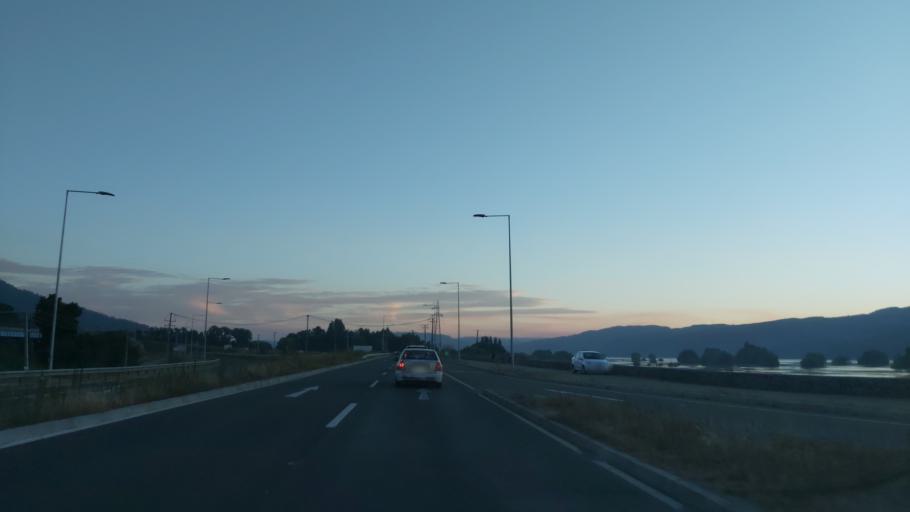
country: CL
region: Biobio
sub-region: Provincia de Concepcion
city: Chiguayante
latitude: -36.8914
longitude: -73.0367
